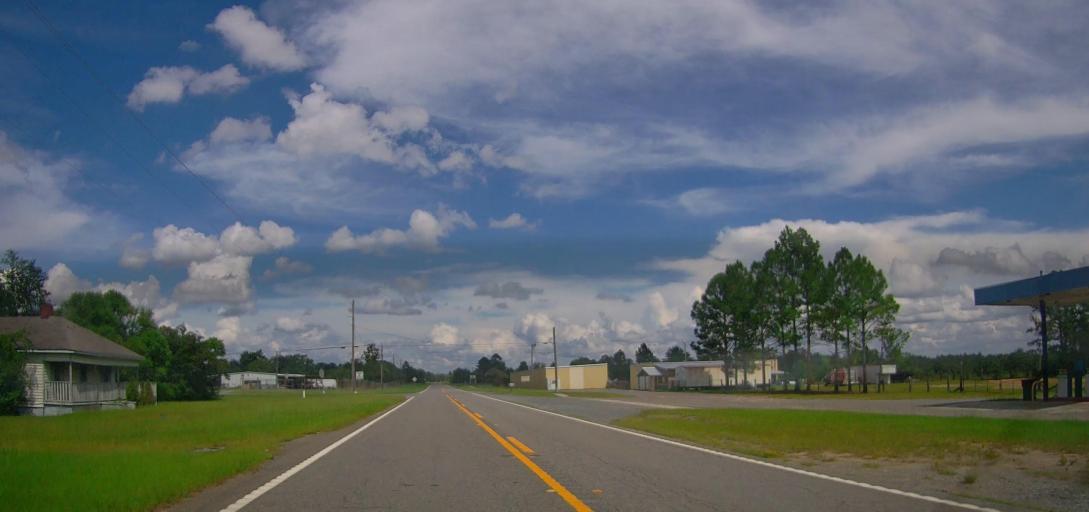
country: US
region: Georgia
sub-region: Taylor County
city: Butler
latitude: 32.5549
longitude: -84.2593
